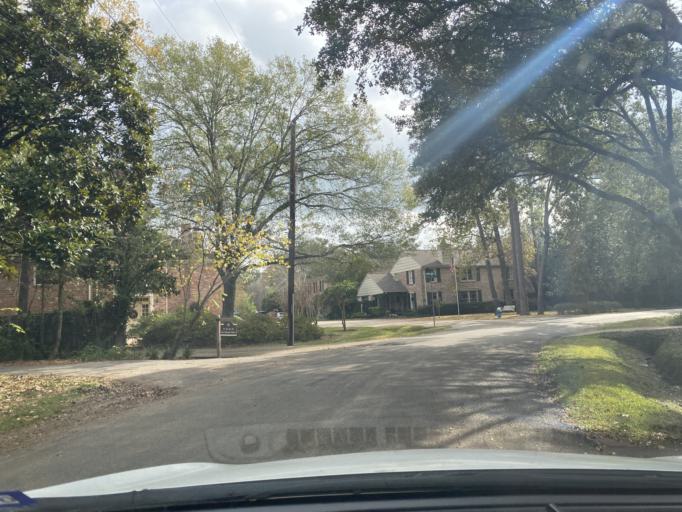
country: US
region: Texas
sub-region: Harris County
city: Hunters Creek Village
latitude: 29.7658
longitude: -95.4729
